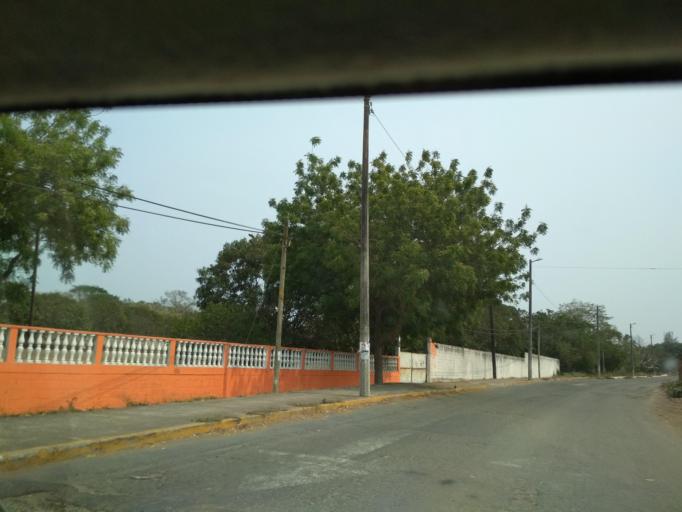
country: MX
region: Veracruz
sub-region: Veracruz
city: Delfino Victoria (Santa Fe)
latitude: 19.2028
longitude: -96.2744
